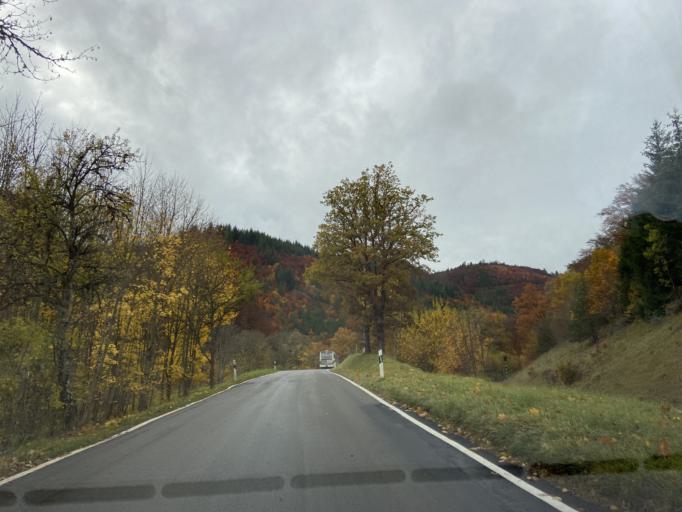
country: DE
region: Baden-Wuerttemberg
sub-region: Tuebingen Region
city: Stetten am Kalten Markt
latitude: 48.0809
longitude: 9.0856
